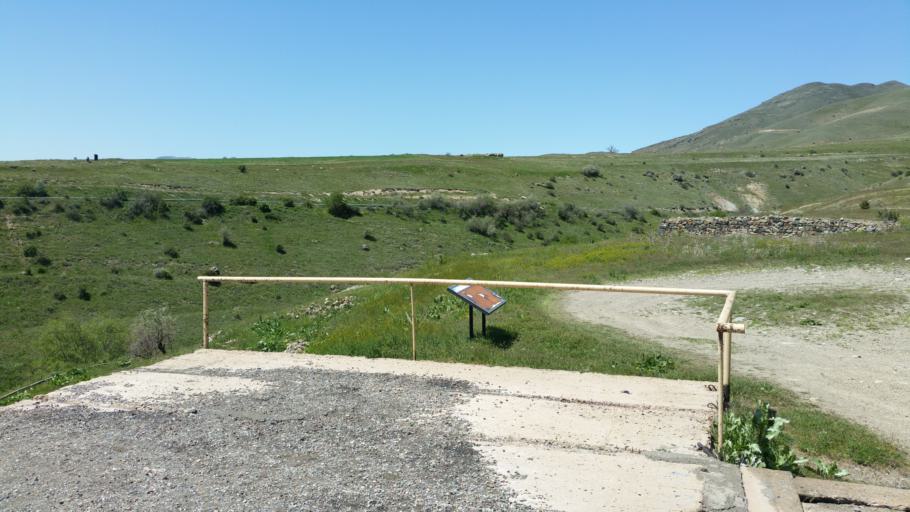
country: AM
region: Vayots' Dzori Marz
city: Vernashen
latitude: 39.7803
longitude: 45.3991
